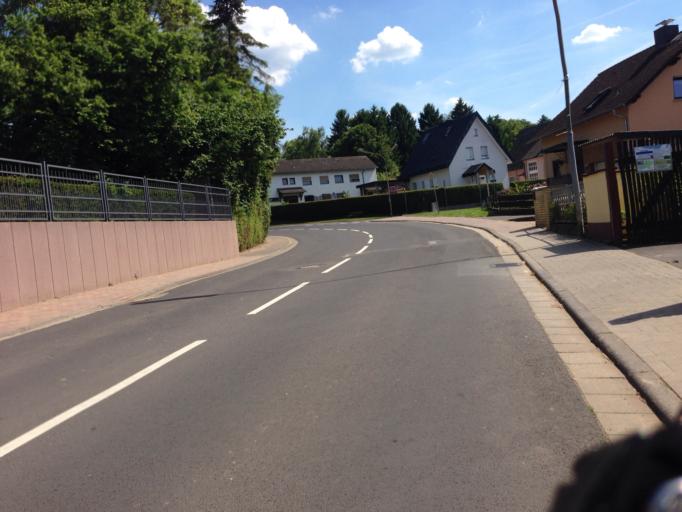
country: DE
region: Hesse
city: Nidderau
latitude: 50.2252
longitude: 8.9123
